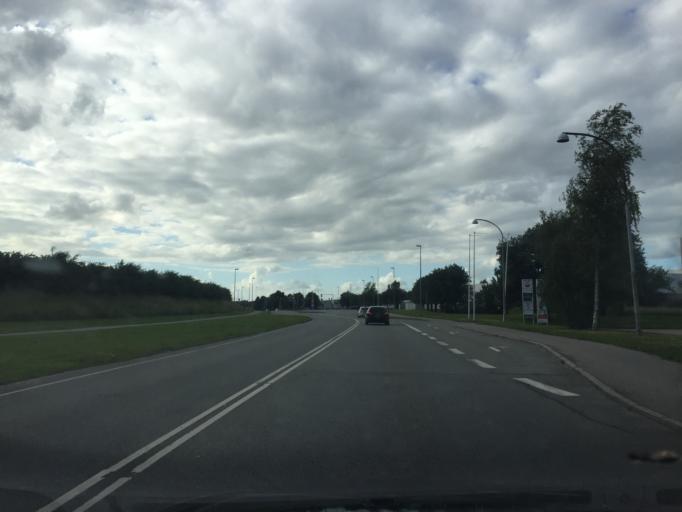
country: DK
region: Capital Region
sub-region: Albertslund Kommune
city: Albertslund
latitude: 55.6503
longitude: 12.3716
